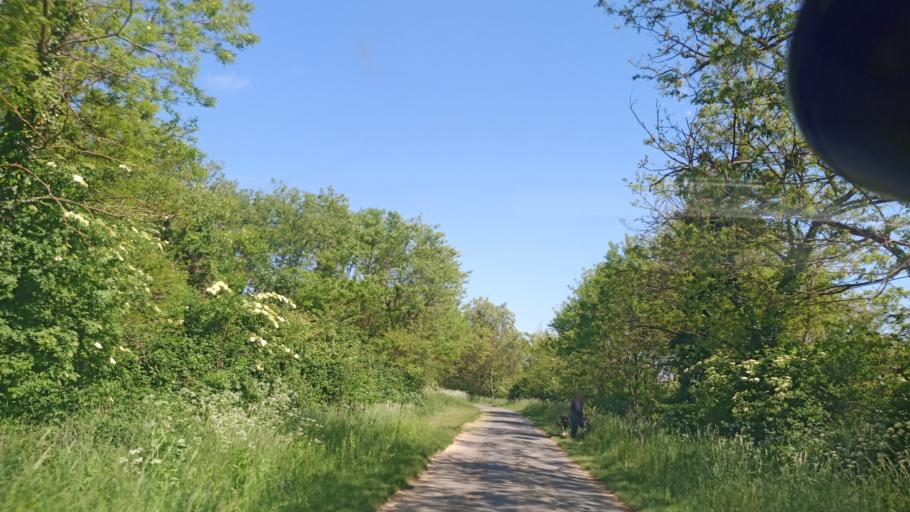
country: HU
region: Zala
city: Pacsa
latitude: 46.6392
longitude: 17.0623
